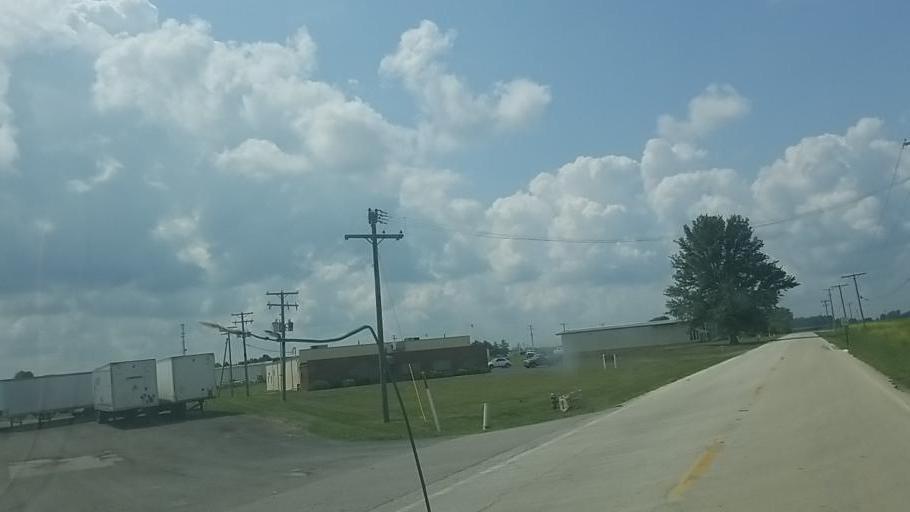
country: US
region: Ohio
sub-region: Wyandot County
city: Upper Sandusky
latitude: 40.8551
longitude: -83.2759
